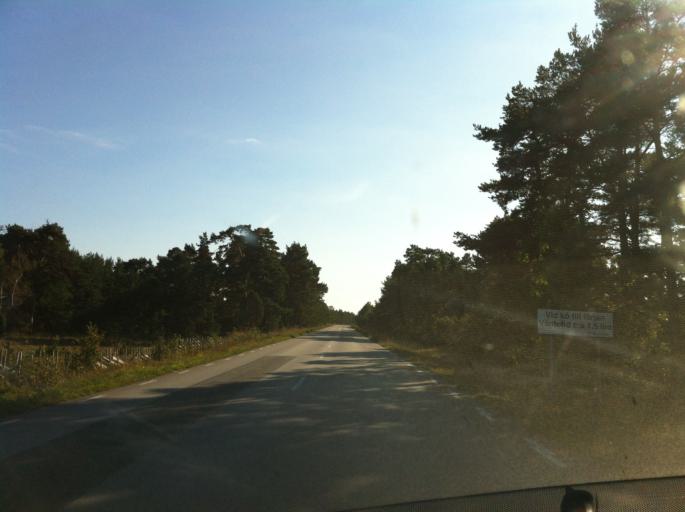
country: SE
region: Gotland
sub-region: Gotland
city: Slite
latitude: 57.8899
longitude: 19.0903
